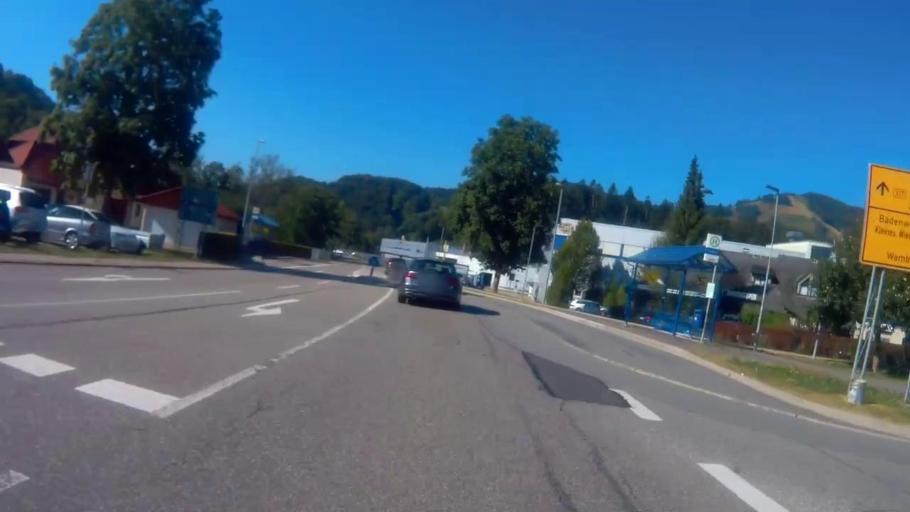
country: DE
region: Baden-Wuerttemberg
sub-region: Freiburg Region
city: Wembach
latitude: 47.7729
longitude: 7.8878
